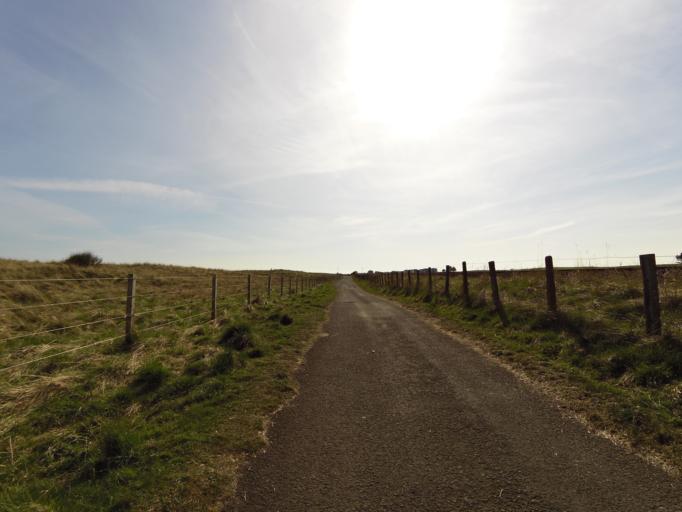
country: GB
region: Scotland
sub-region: Angus
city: Arbroath
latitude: 56.5376
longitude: -2.6273
